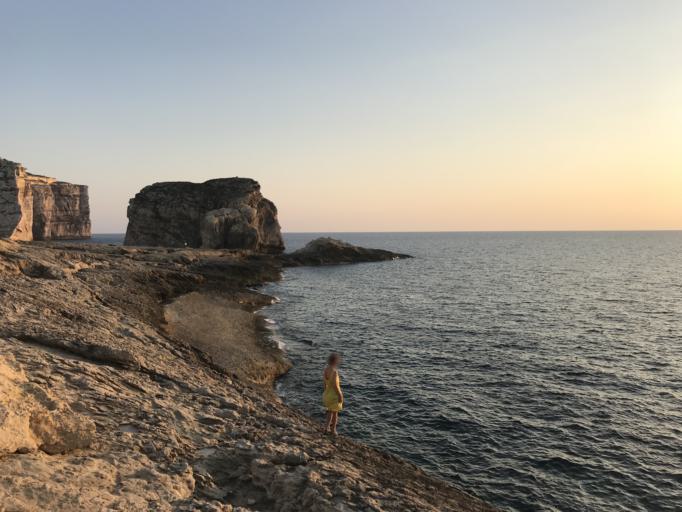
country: MT
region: Saint Lawrence
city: San Lawrenz
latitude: 36.0499
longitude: 14.1905
